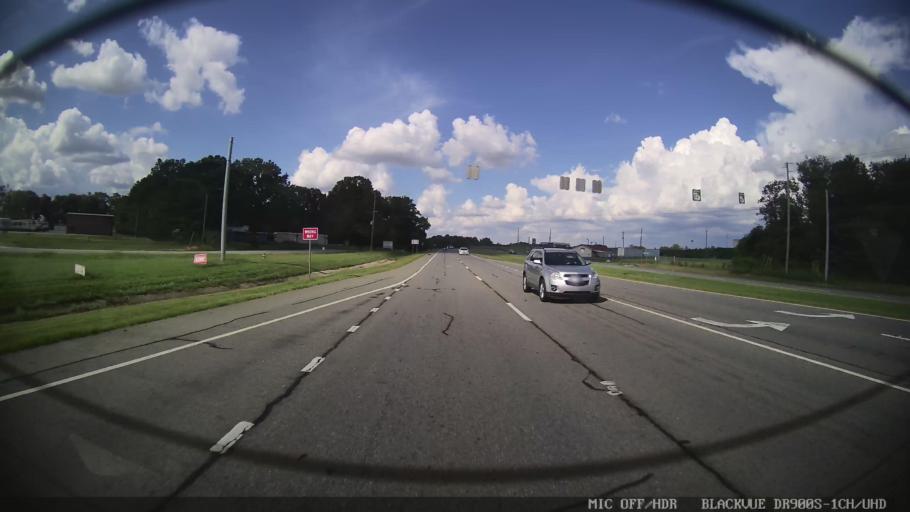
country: US
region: Georgia
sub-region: Bartow County
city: Cartersville
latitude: 34.1298
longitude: -84.8517
